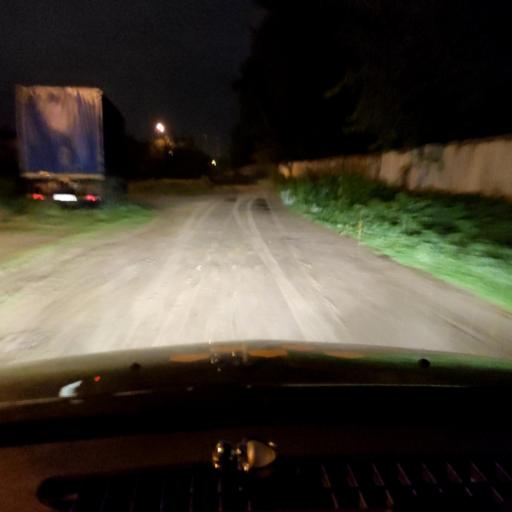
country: RU
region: Voronezj
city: Maslovka
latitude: 51.6060
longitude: 39.2247
